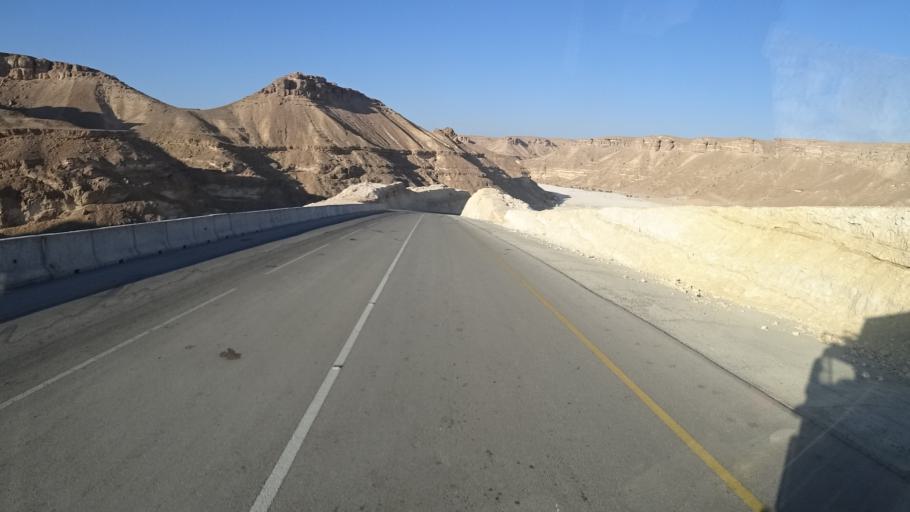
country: YE
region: Al Mahrah
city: Hawf
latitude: 17.0950
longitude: 53.0462
